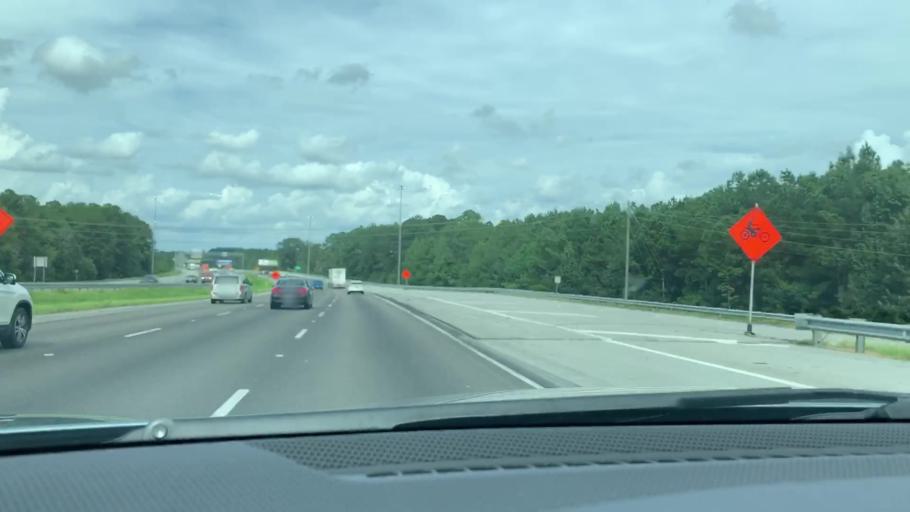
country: US
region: Georgia
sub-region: Liberty County
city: Midway
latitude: 31.6551
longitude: -81.3941
